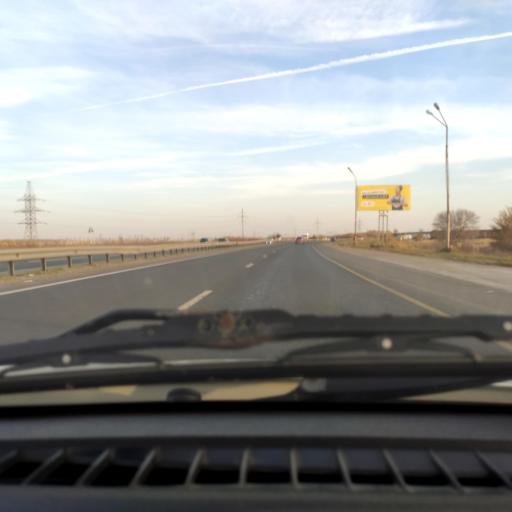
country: RU
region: Samara
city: Tol'yatti
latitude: 53.5669
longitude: 49.4920
